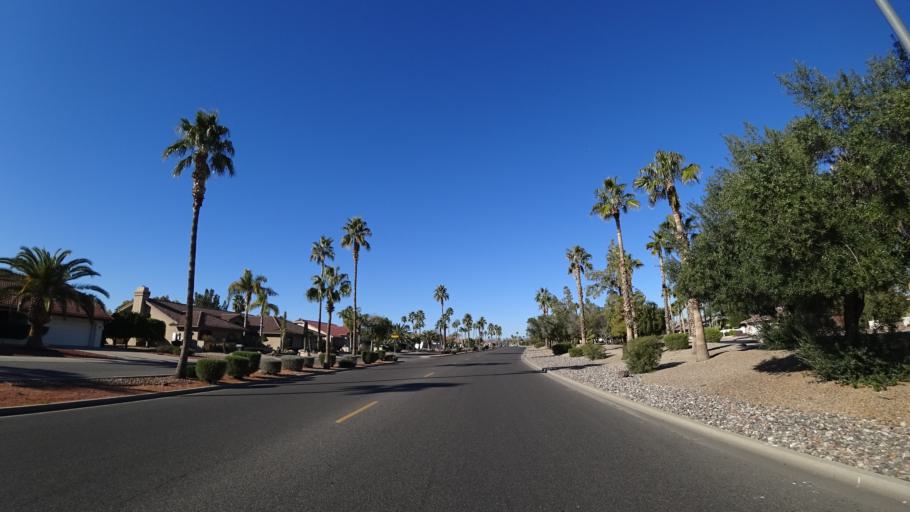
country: US
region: Arizona
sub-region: Maricopa County
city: Sun City West
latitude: 33.6740
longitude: -112.3542
